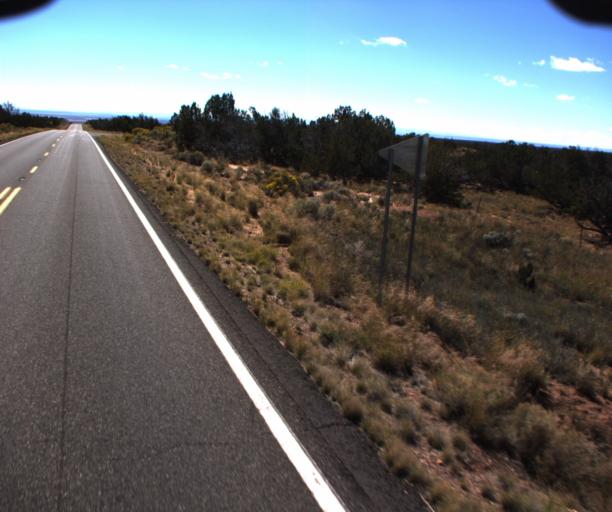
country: US
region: Arizona
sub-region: Apache County
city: Saint Johns
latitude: 34.8406
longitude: -109.2376
